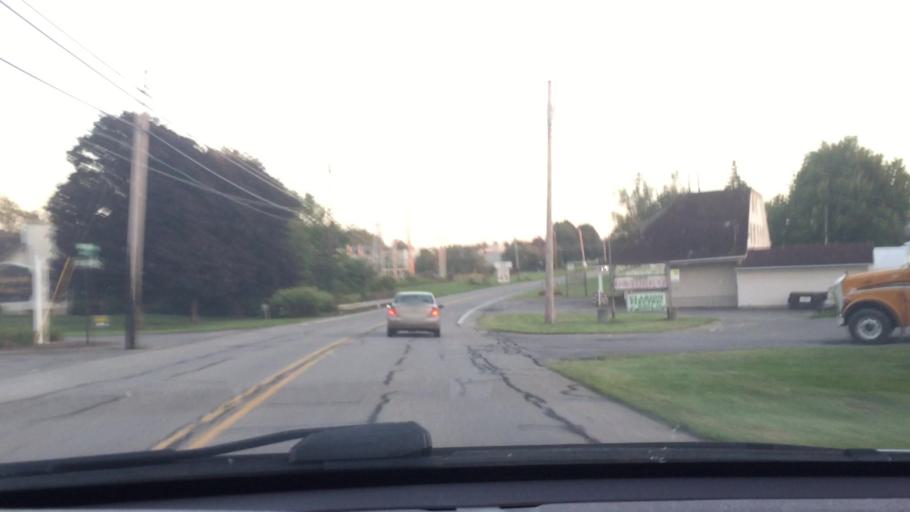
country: US
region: Pennsylvania
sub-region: Mercer County
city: Grove City
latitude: 41.1490
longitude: -80.0822
